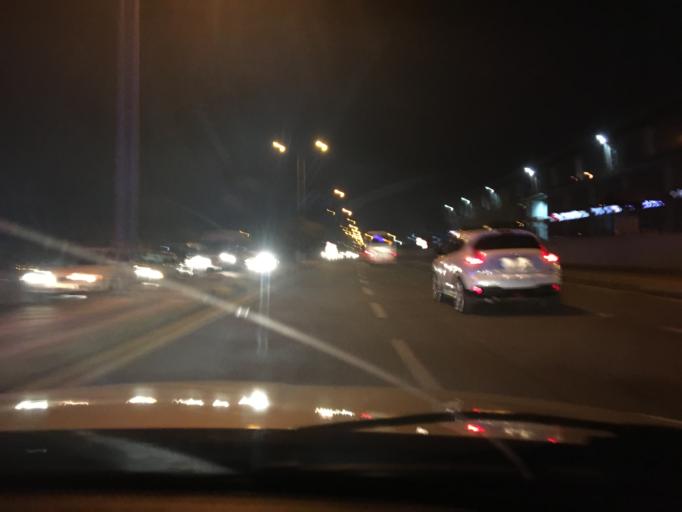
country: TR
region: Gaziantep
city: Gaziantep
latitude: 37.0930
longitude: 37.4010
